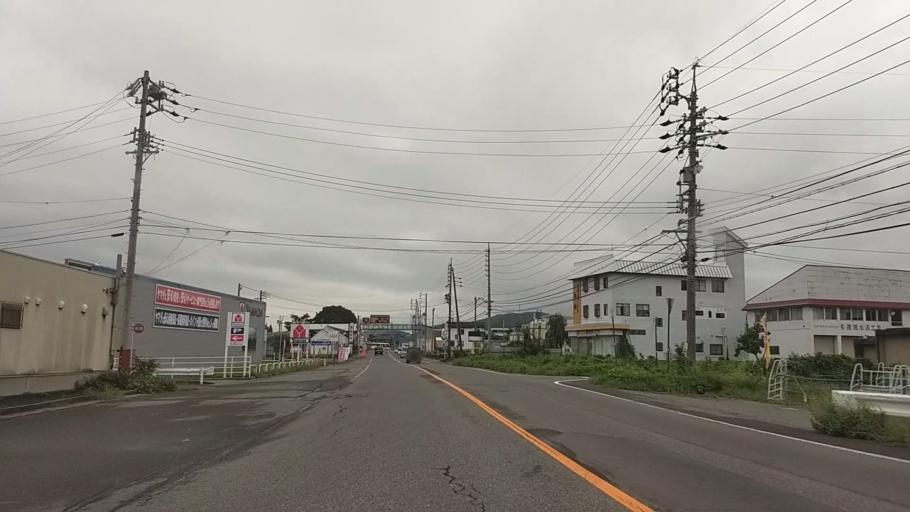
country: JP
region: Nagano
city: Iiyama
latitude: 36.8298
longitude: 138.3546
